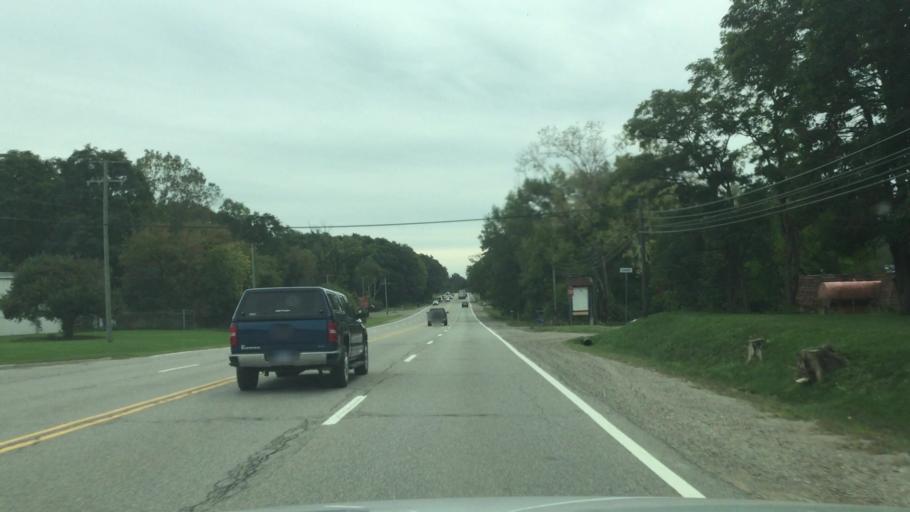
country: US
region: Michigan
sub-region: Oakland County
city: Clarkston
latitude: 42.7706
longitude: -83.4901
